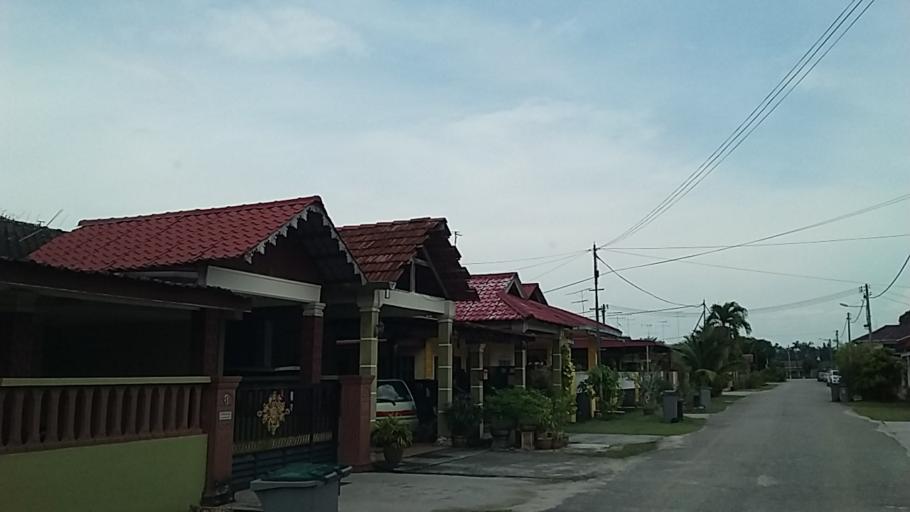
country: MY
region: Johor
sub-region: Daerah Batu Pahat
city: Batu Pahat
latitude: 1.7532
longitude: 103.0291
